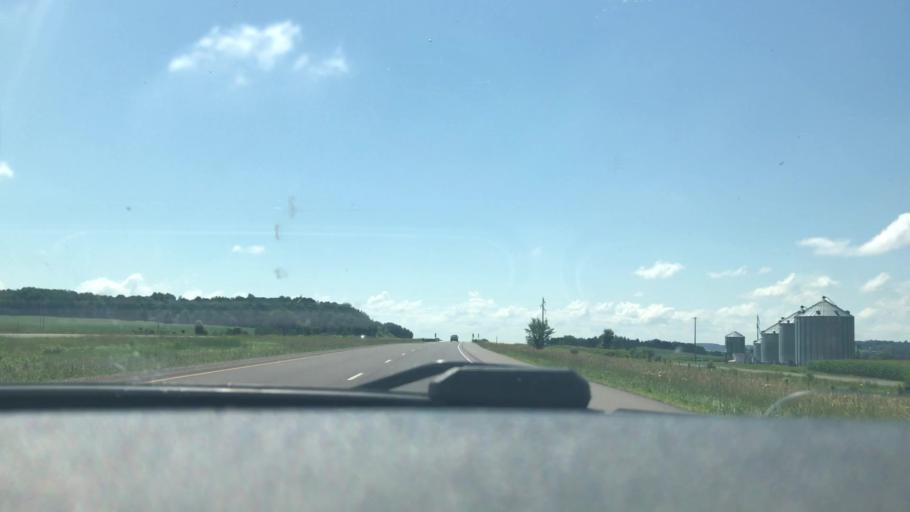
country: US
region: Wisconsin
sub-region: Chippewa County
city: Bloomer
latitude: 45.0341
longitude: -91.4528
